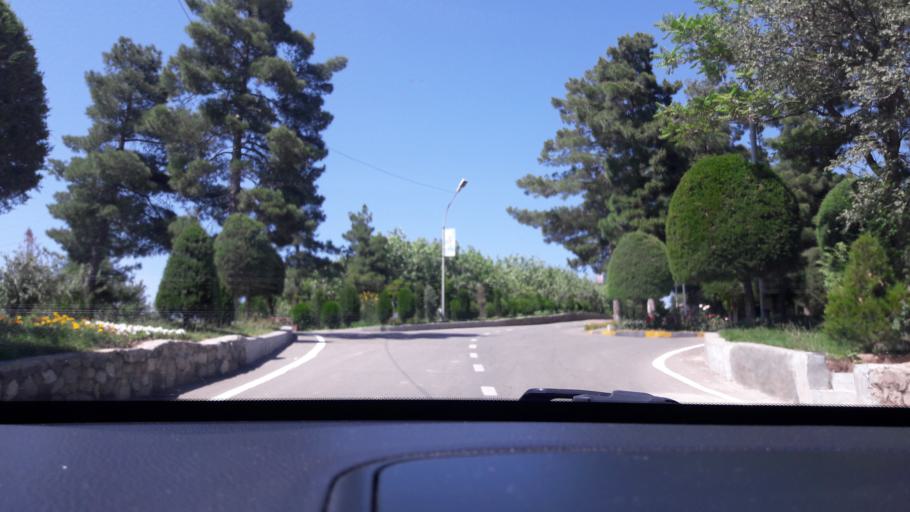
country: TJ
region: Dushanbe
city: Dushanbe
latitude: 38.5801
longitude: 68.8112
